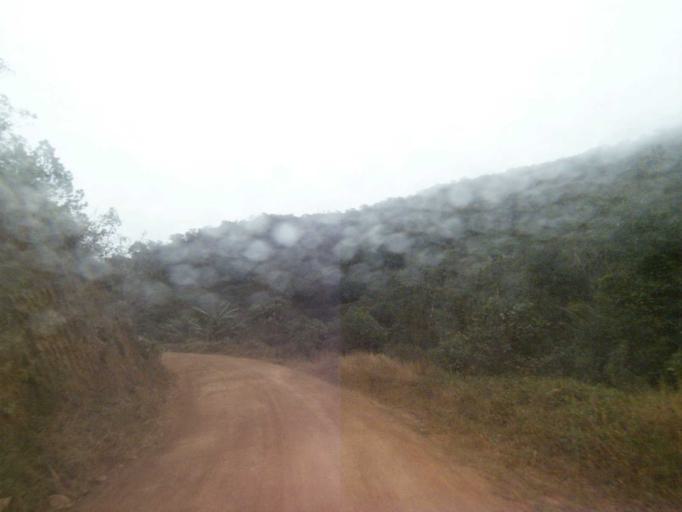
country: BR
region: Santa Catarina
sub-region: Anitapolis
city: Anitapolis
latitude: -27.8891
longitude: -49.1317
